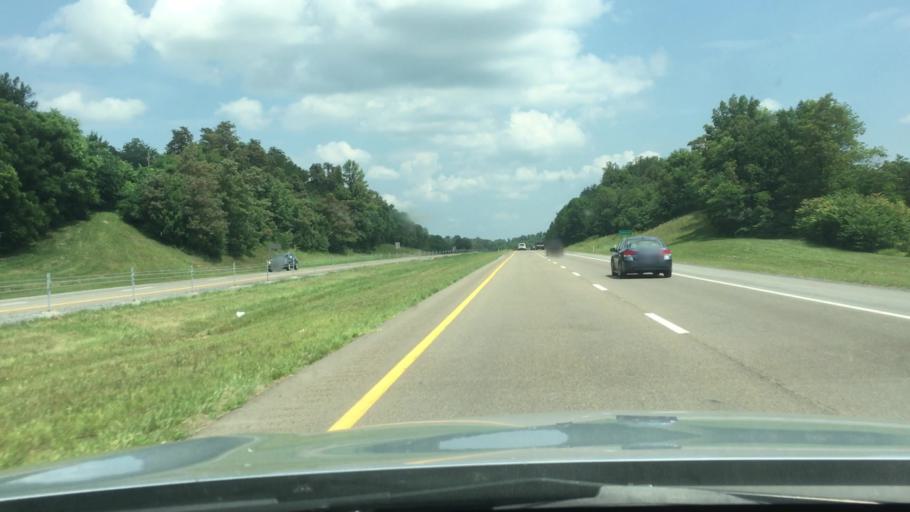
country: US
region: Tennessee
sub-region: Carter County
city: Pine Crest
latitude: 36.2583
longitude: -82.3226
